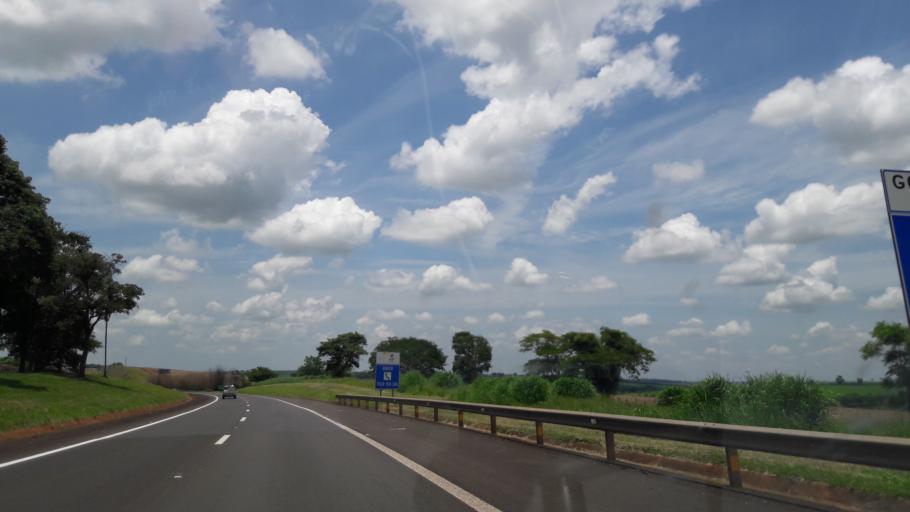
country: BR
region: Sao Paulo
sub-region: Avare
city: Avare
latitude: -22.9545
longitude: -48.8253
